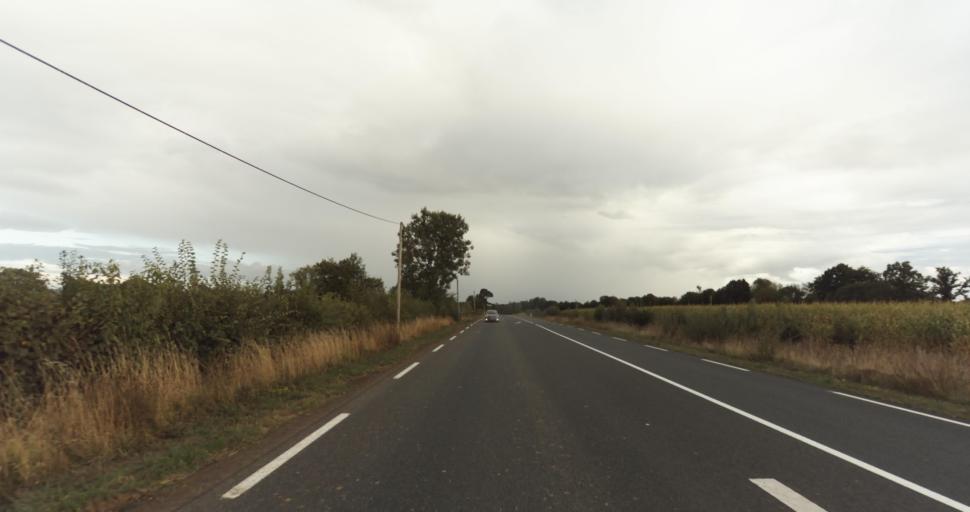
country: FR
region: Lower Normandy
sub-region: Departement de l'Orne
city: Gace
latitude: 48.8515
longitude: 0.2570
